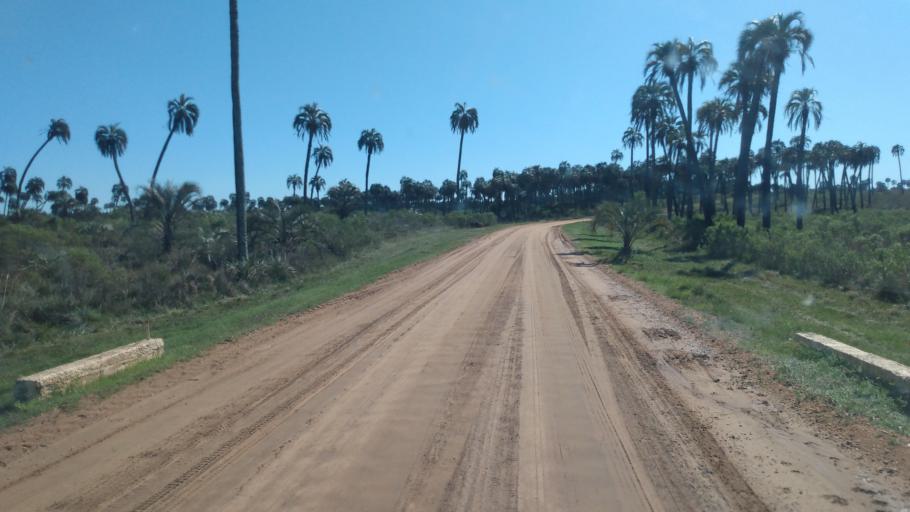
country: AR
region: Entre Rios
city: Ubajay
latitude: -31.8525
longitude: -58.3153
